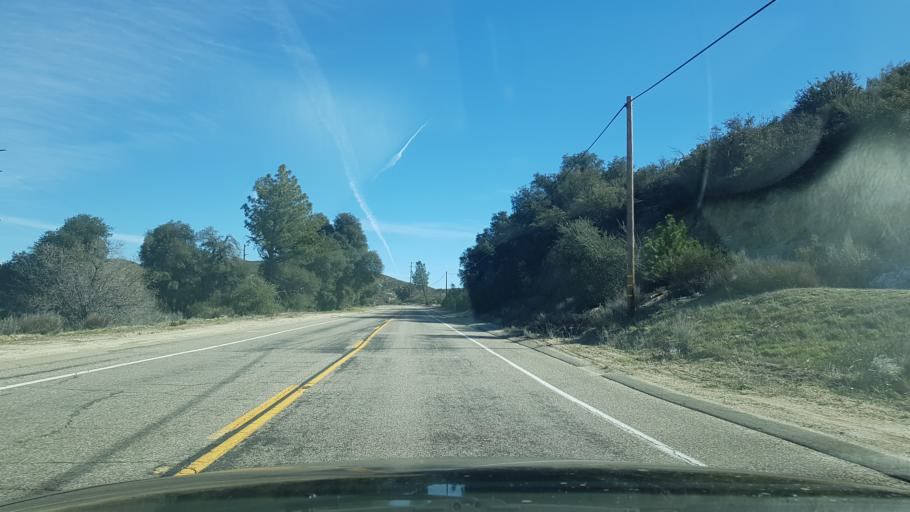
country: US
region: California
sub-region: San Diego County
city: Julian
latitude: 33.2146
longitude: -116.5684
